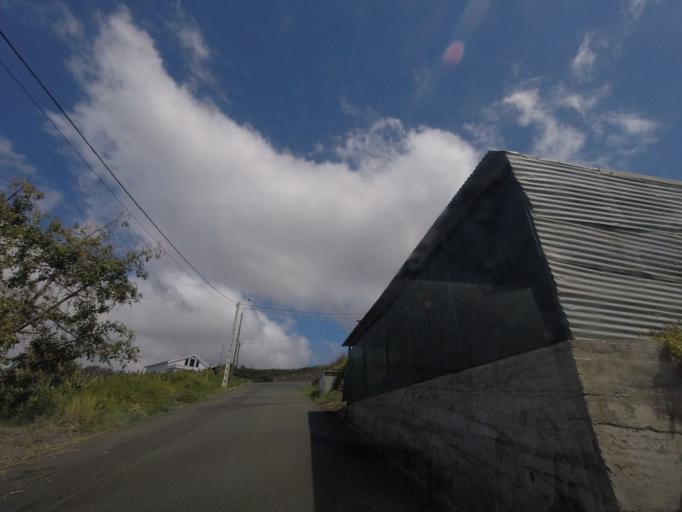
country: PT
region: Madeira
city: Ponta do Sol
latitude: 32.6838
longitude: -17.0818
